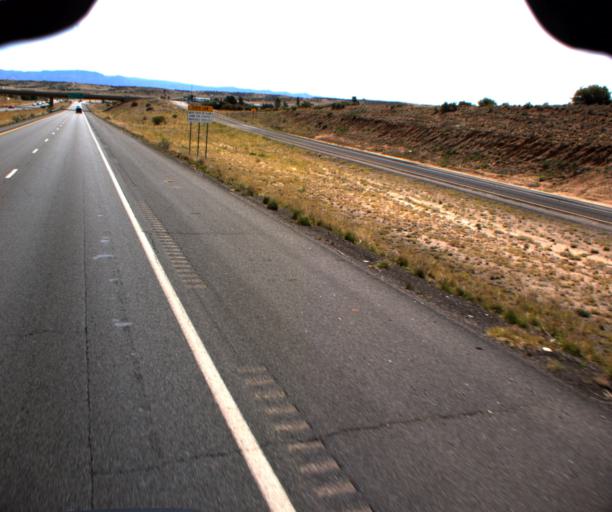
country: US
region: Arizona
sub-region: Yavapai County
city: Prescott
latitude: 34.6341
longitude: -112.4205
